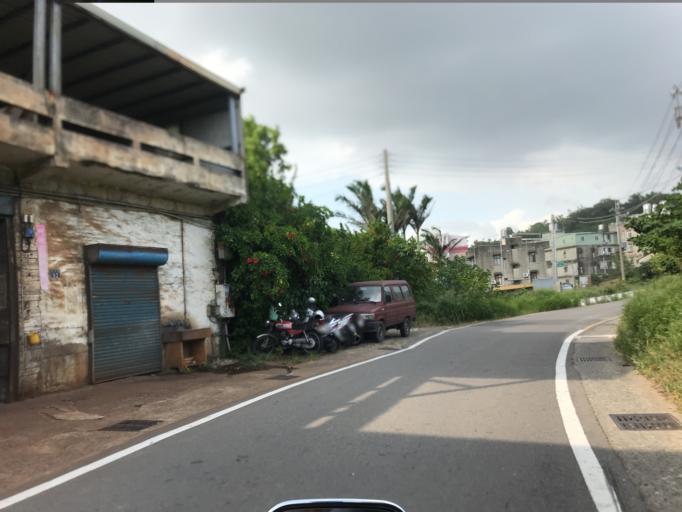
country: TW
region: Taiwan
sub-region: Hsinchu
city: Hsinchu
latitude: 24.7799
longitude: 120.9321
